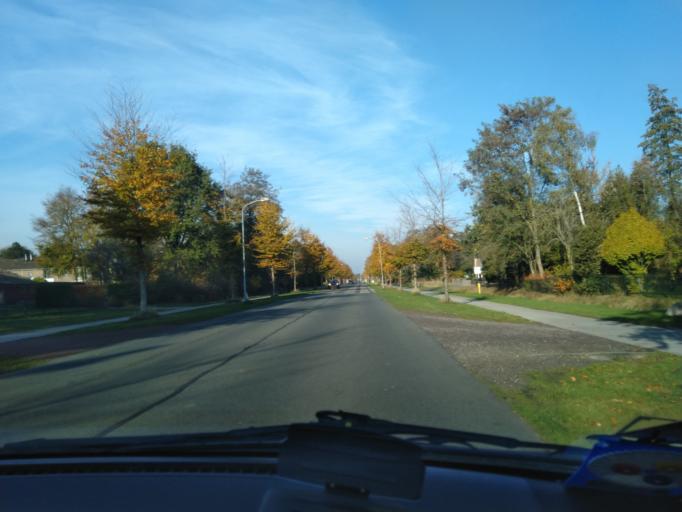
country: NL
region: Drenthe
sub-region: Gemeente Tynaarlo
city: Vries
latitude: 53.0650
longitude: 6.5769
